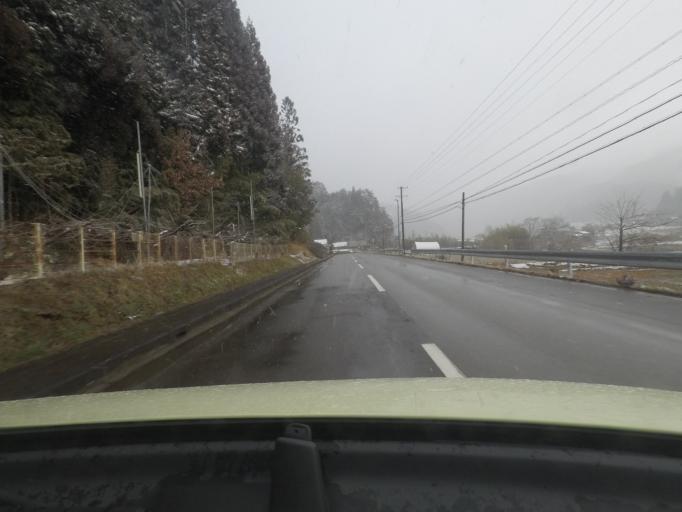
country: JP
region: Gifu
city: Takayama
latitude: 36.1411
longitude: 137.3103
